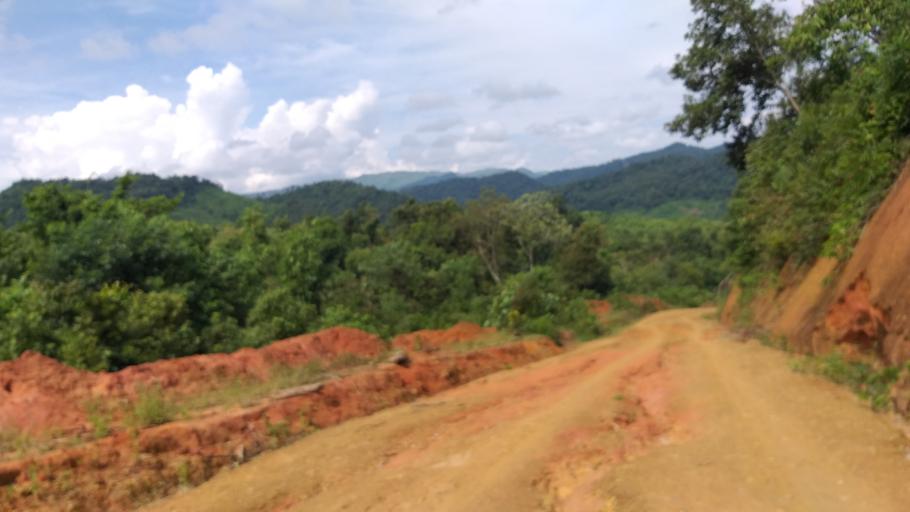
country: VN
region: Huyen Dien Bien
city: Dien Bien Phu
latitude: 21.5049
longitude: 102.6702
